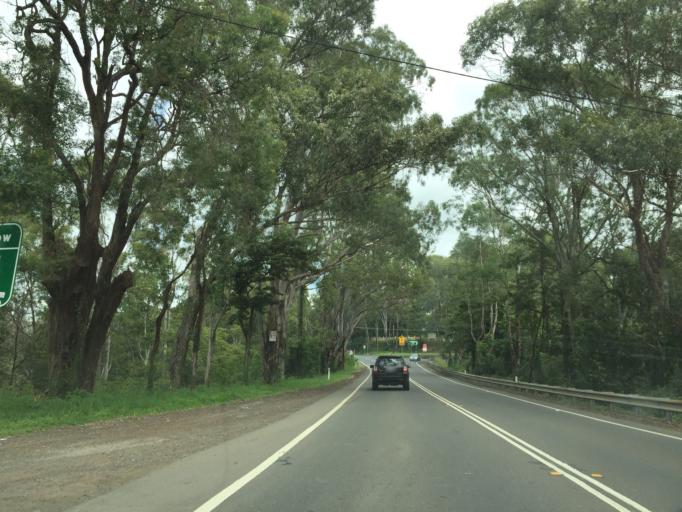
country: AU
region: New South Wales
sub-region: Hawkesbury
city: Richmond
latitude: -33.5484
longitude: 150.6774
